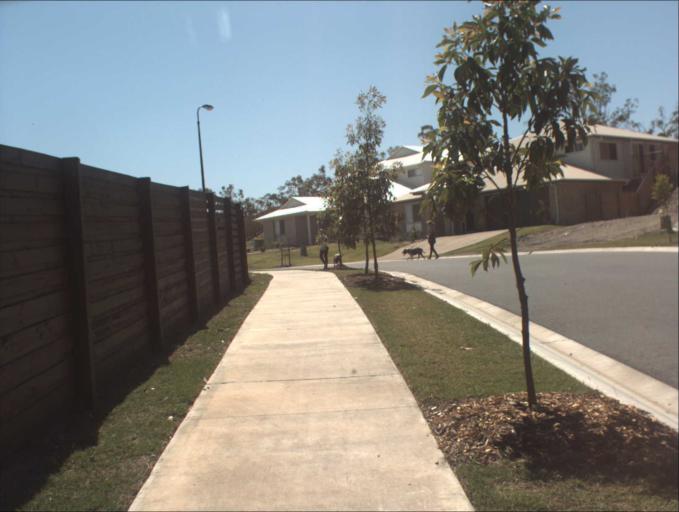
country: AU
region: Queensland
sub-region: Logan
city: Waterford West
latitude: -27.7175
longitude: 153.1566
